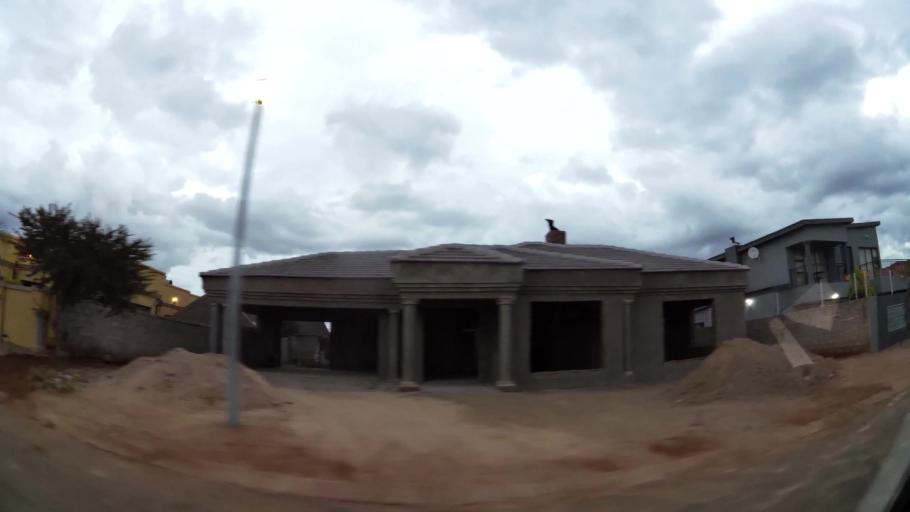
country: ZA
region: Limpopo
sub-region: Waterberg District Municipality
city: Mokopane
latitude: -24.1995
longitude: 28.9957
